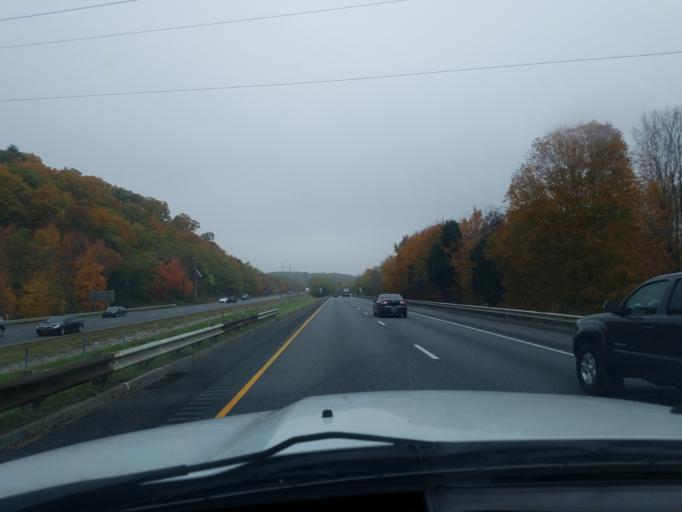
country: US
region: Indiana
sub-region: Floyd County
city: New Albany
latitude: 38.3014
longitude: -85.8624
